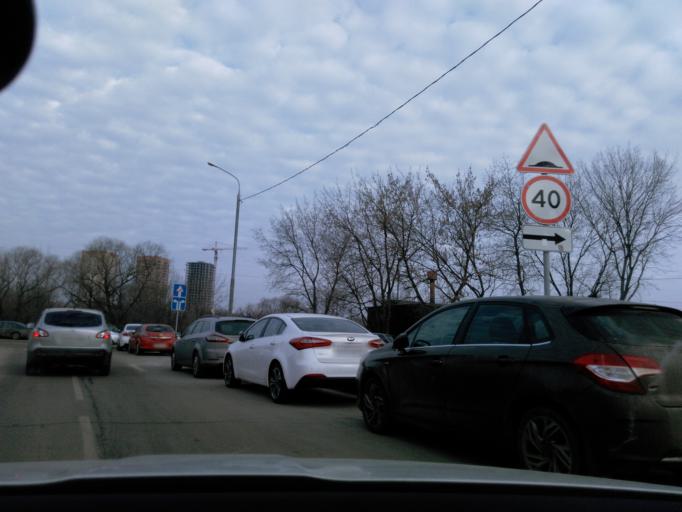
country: RU
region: Moskovskaya
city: Levoberezhnaya
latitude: 55.9002
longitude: 37.4741
